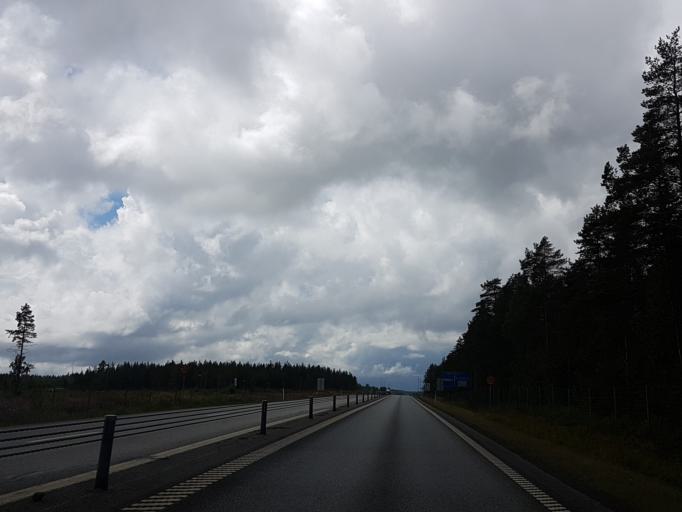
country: SE
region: Vaesterbotten
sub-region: Umea Kommun
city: Taftea
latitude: 63.8639
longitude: 20.4224
